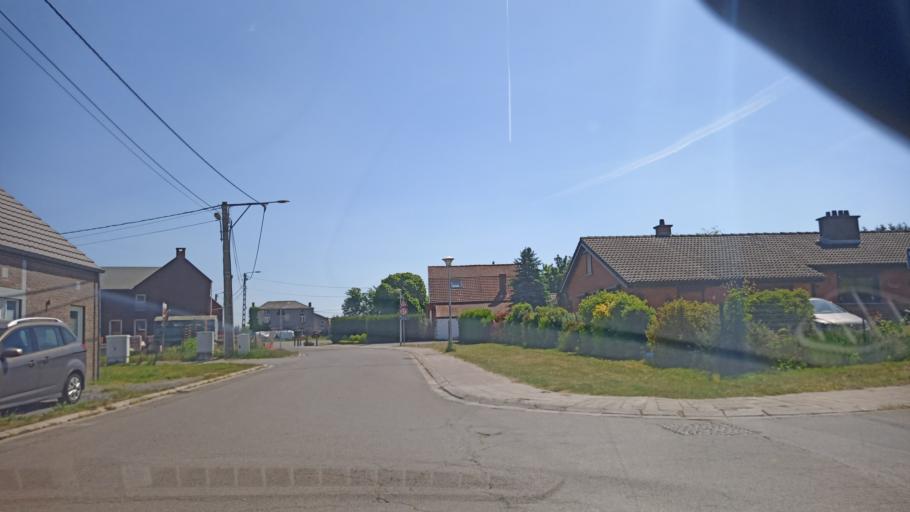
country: BE
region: Wallonia
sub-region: Province du Hainaut
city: Lobbes
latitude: 50.3254
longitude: 4.2513
